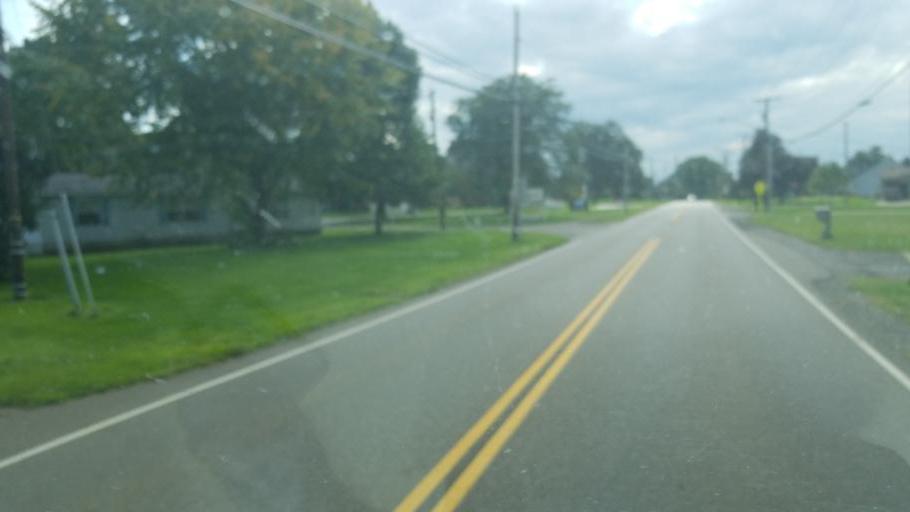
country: US
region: Ohio
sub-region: Carroll County
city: Lake Mohawk
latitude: 40.6665
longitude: -81.2662
